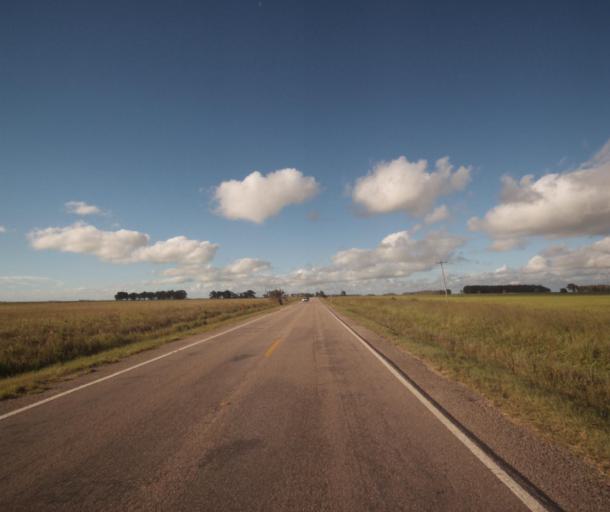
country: BR
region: Rio Grande do Sul
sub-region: Arroio Grande
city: Arroio Grande
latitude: -32.4522
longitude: -52.5709
